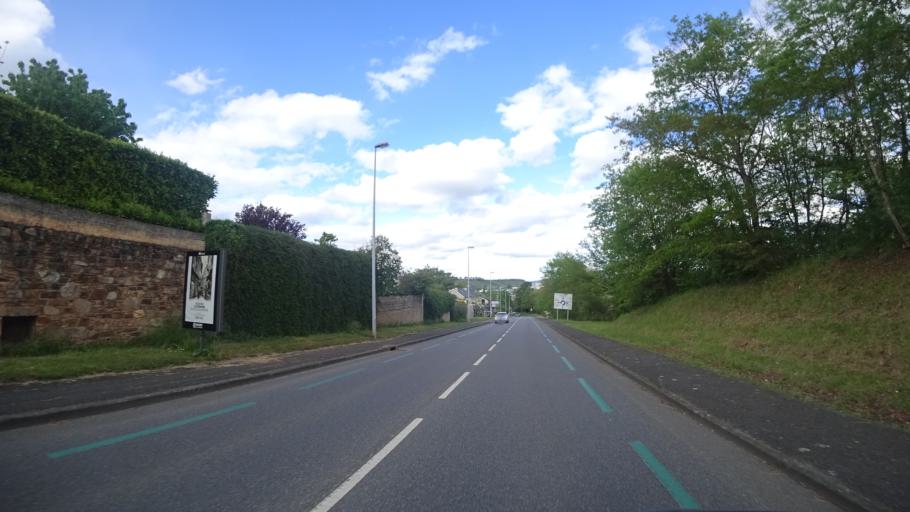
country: FR
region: Midi-Pyrenees
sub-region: Departement de l'Aveyron
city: Rodez
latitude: 44.3578
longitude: 2.5894
